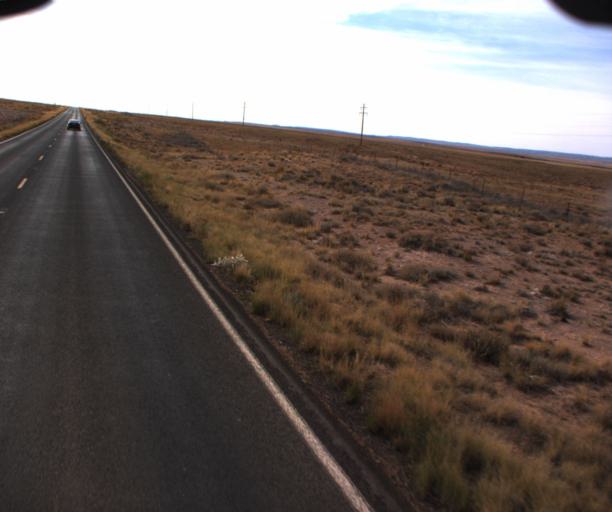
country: US
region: Arizona
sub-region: Apache County
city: Chinle
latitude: 35.9792
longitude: -109.5998
